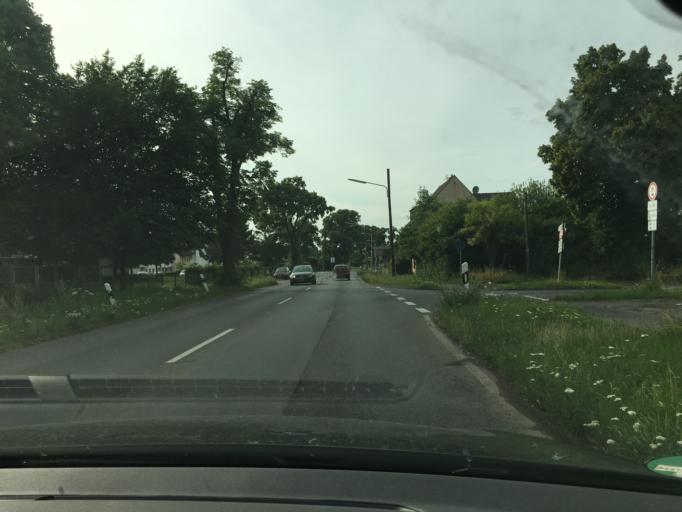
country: DE
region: North Rhine-Westphalia
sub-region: Regierungsbezirk Koln
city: Bonn
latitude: 50.7628
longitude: 7.0567
